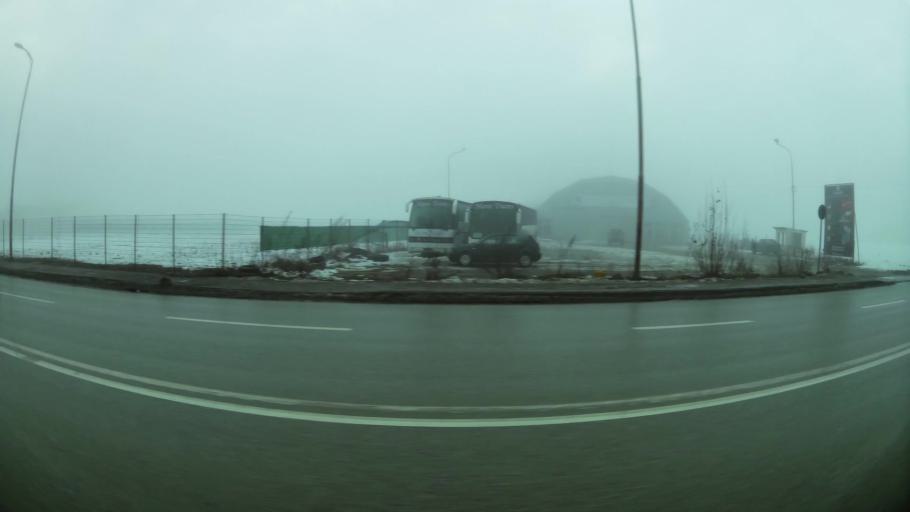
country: XK
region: Pristina
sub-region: Komuna e Prishtines
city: Pristina
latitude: 42.6579
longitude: 21.1398
